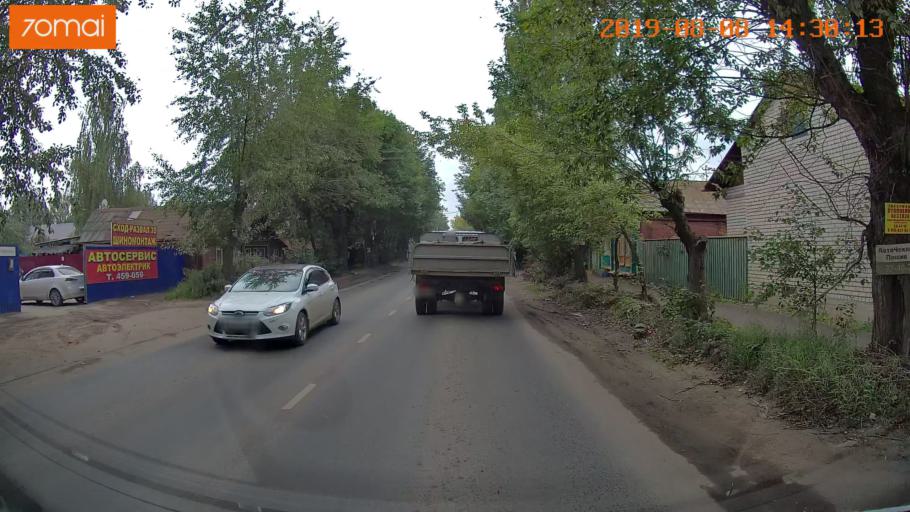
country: RU
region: Ivanovo
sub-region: Gorod Ivanovo
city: Ivanovo
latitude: 56.9916
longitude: 40.9528
